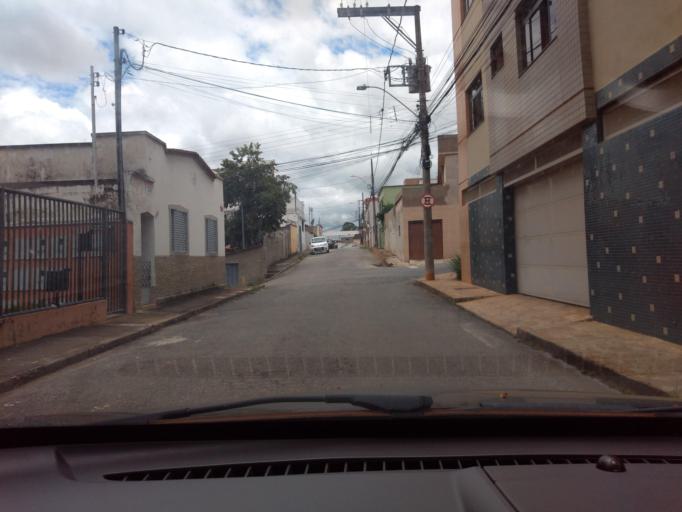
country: BR
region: Minas Gerais
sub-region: Lavras
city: Lavras
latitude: -21.2397
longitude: -44.9959
